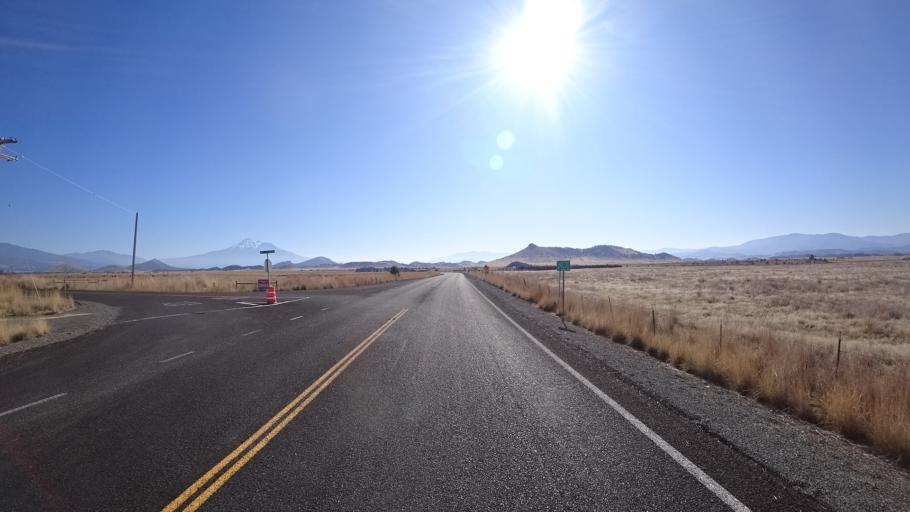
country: US
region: California
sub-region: Siskiyou County
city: Montague
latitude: 41.7248
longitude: -122.4573
